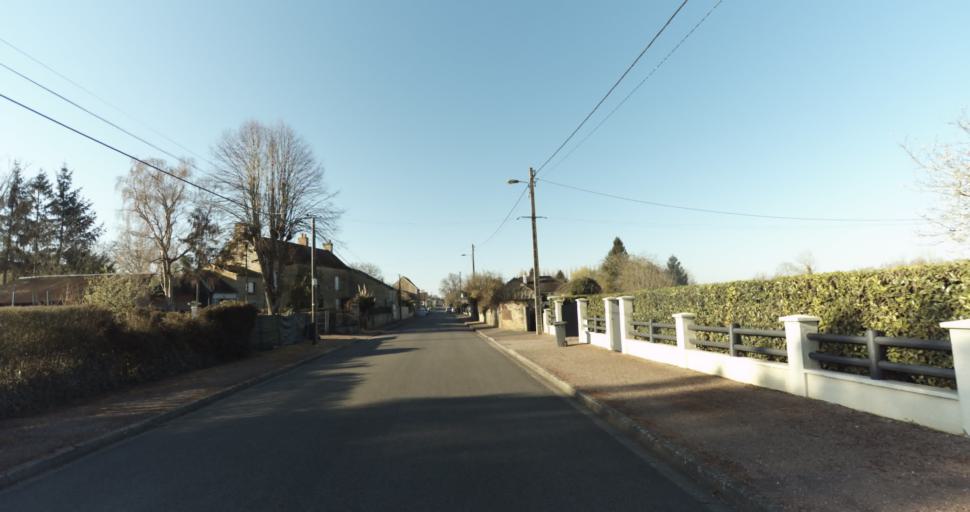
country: FR
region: Lower Normandy
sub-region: Departement du Calvados
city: Saint-Pierre-sur-Dives
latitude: 49.0278
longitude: -0.0266
